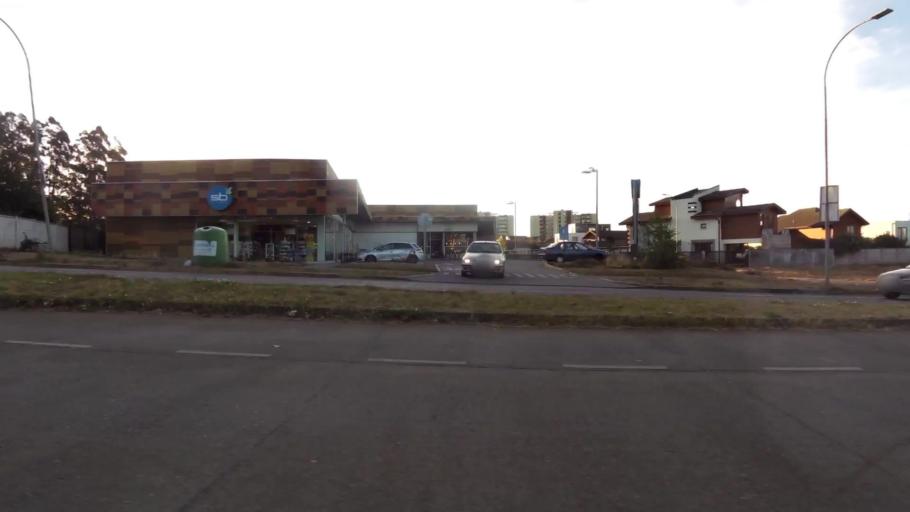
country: CL
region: Biobio
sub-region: Provincia de Concepcion
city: Concepcion
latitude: -36.8496
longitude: -73.0928
